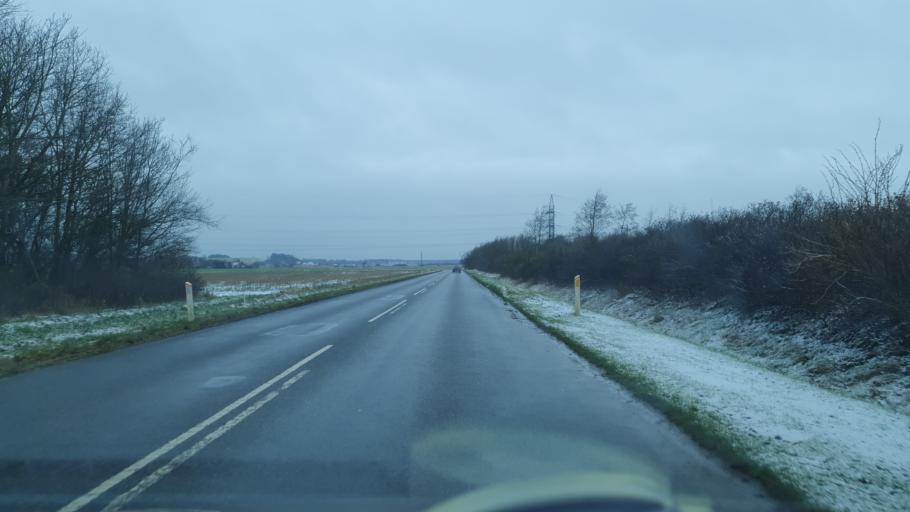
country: DK
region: North Denmark
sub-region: Jammerbugt Kommune
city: Brovst
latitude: 57.1121
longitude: 9.5007
